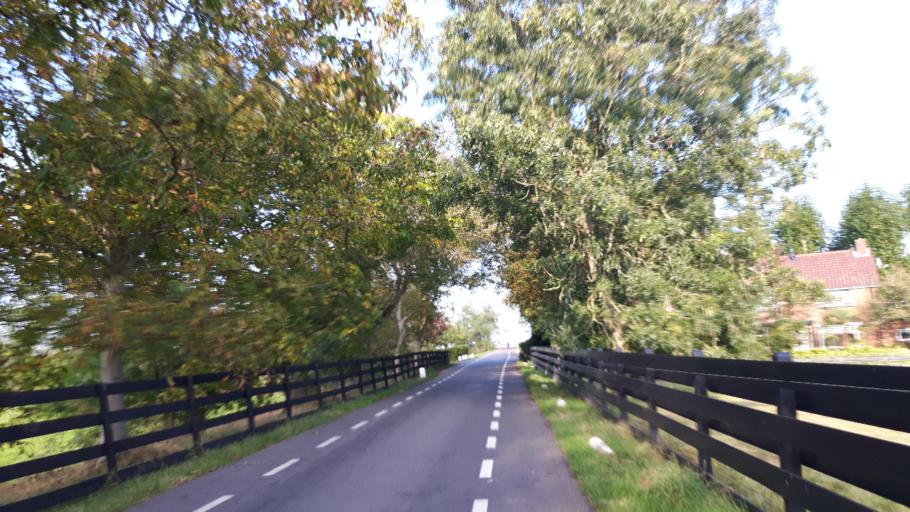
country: NL
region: Utrecht
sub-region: Gemeente Oudewater
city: Oudewater
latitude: 52.0254
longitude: 4.8947
